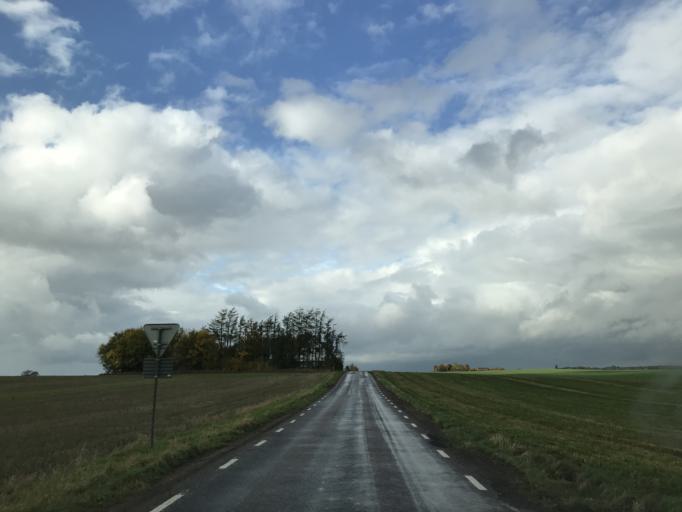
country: SE
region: Skane
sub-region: Svalovs Kommun
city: Svaloev
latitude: 55.9014
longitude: 13.1887
